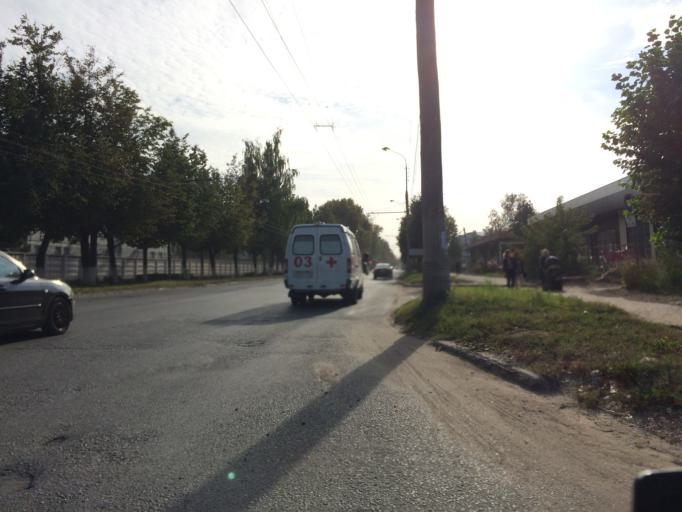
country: RU
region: Mariy-El
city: Yoshkar-Ola
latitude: 56.6333
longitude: 47.8561
